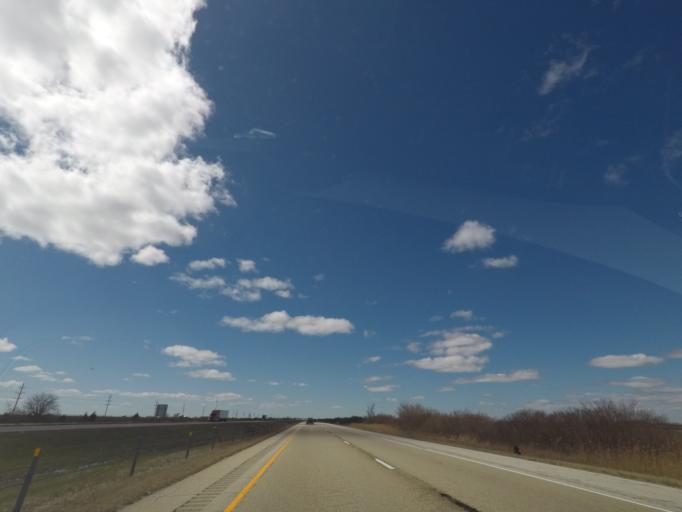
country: US
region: Illinois
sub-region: Grundy County
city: Gardner
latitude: 41.1713
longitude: -88.3304
